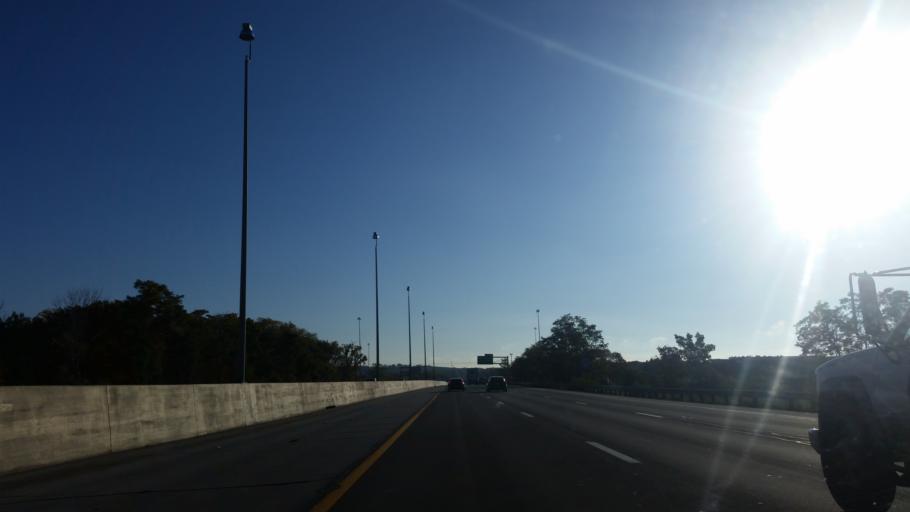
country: US
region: Ohio
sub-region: Summit County
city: Fairlawn
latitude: 41.1193
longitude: -81.6426
